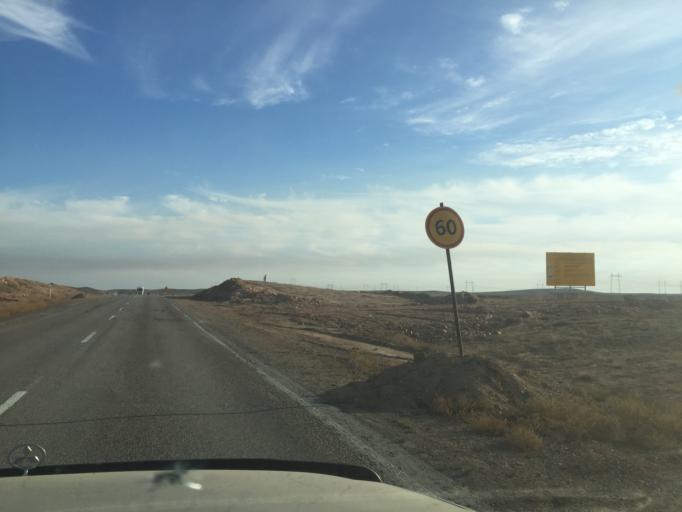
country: KZ
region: Zhambyl
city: Mynaral
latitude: 45.5227
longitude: 73.4867
